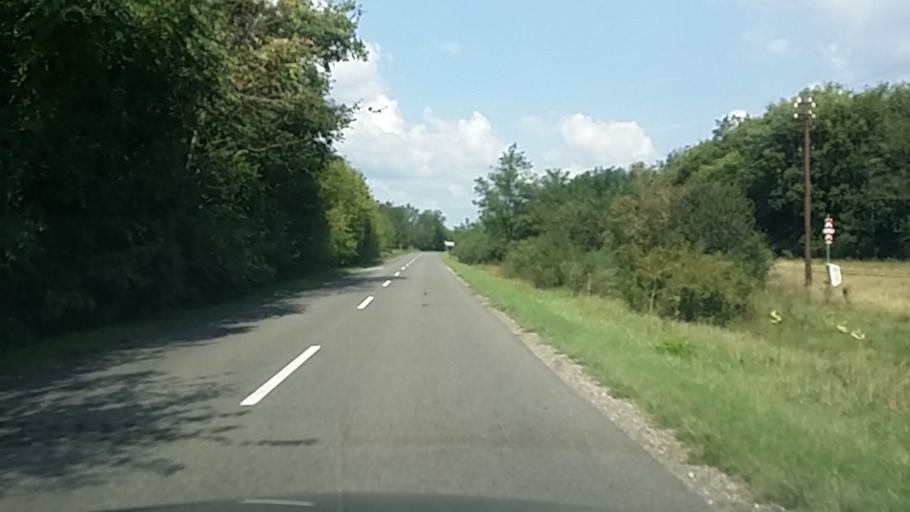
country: HU
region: Bacs-Kiskun
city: Lakitelek
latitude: 46.8492
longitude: 19.9791
